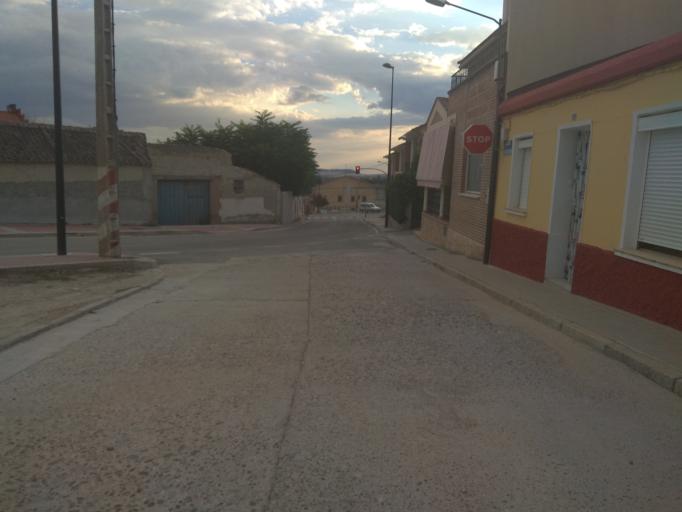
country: ES
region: Castille and Leon
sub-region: Provincia de Valladolid
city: Portillo
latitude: 41.4770
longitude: -4.5949
